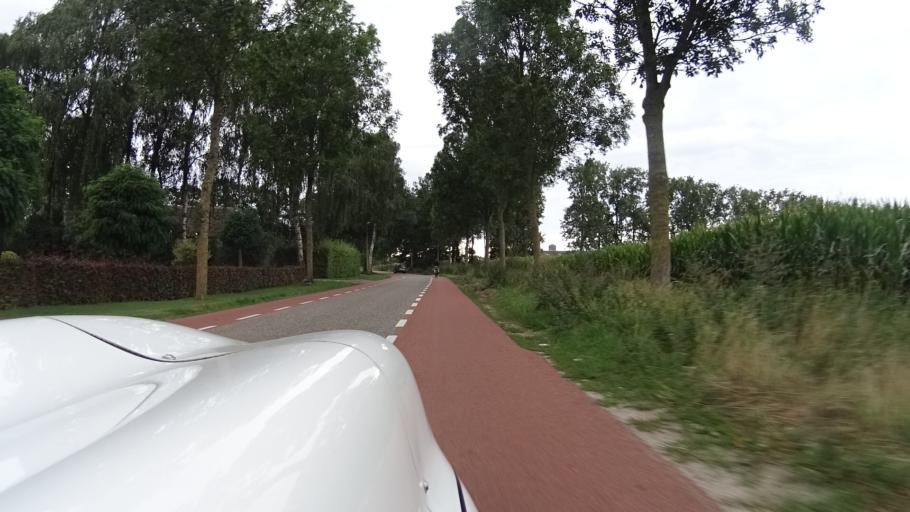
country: NL
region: North Brabant
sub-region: Gemeente Veghel
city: Mariaheide
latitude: 51.6465
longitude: 5.5855
